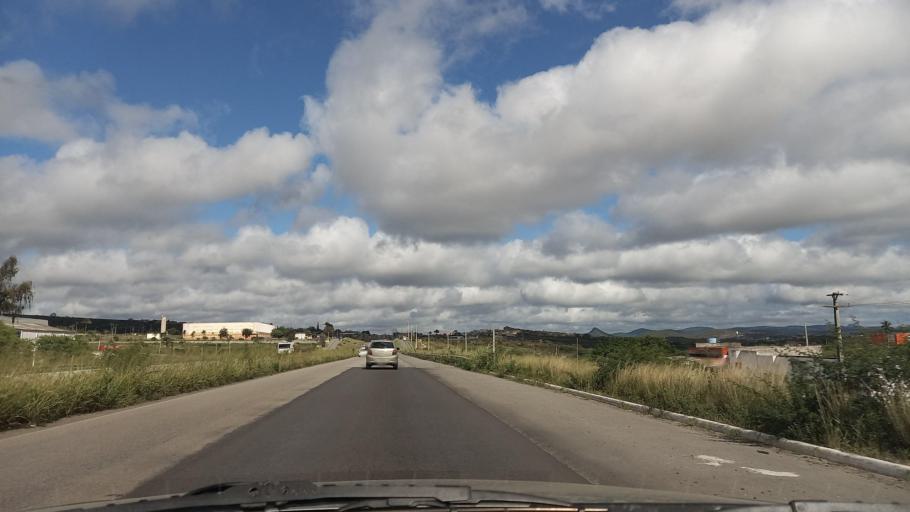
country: BR
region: Pernambuco
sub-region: Caruaru
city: Caruaru
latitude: -8.3042
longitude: -36.0092
